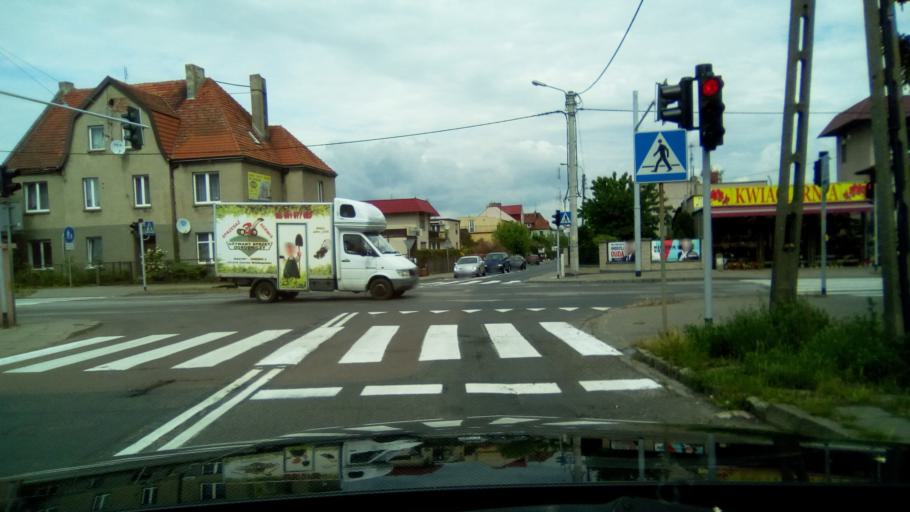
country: PL
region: Greater Poland Voivodeship
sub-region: Powiat gnieznienski
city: Gniezno
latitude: 52.5202
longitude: 17.6053
